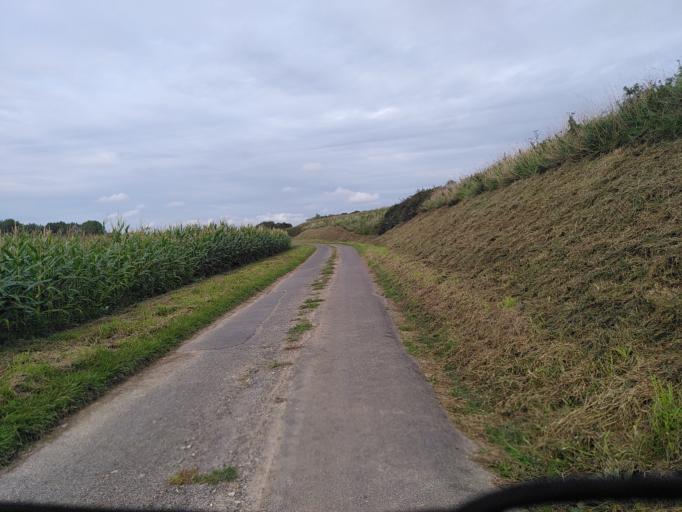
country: FR
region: Nord-Pas-de-Calais
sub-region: Departement du Pas-de-Calais
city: Therouanne
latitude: 50.6059
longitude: 2.1927
